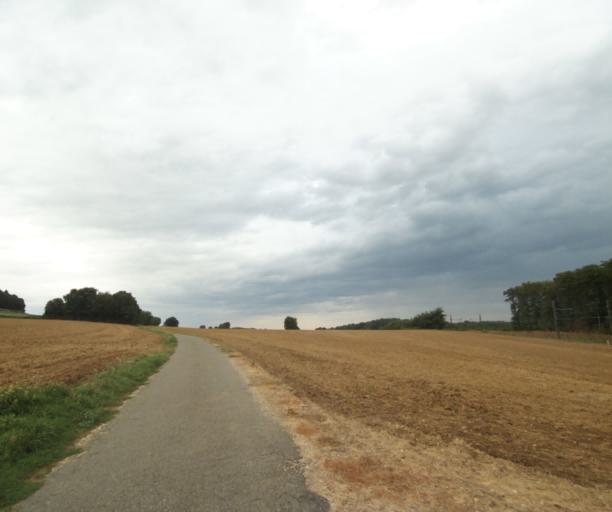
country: FR
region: Bourgogne
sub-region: Departement de Saone-et-Loire
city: Tournus
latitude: 46.5904
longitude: 4.9087
